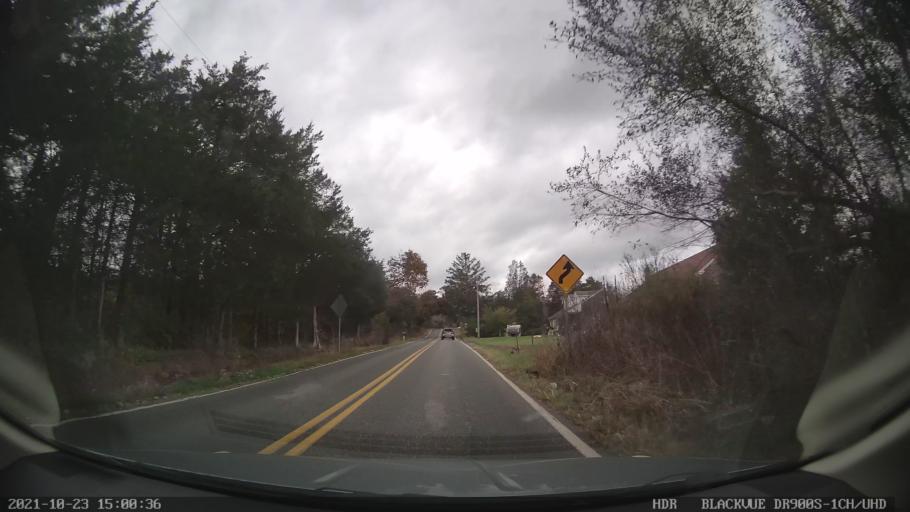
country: US
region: Pennsylvania
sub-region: Montgomery County
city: East Greenville
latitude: 40.3992
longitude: -75.5396
